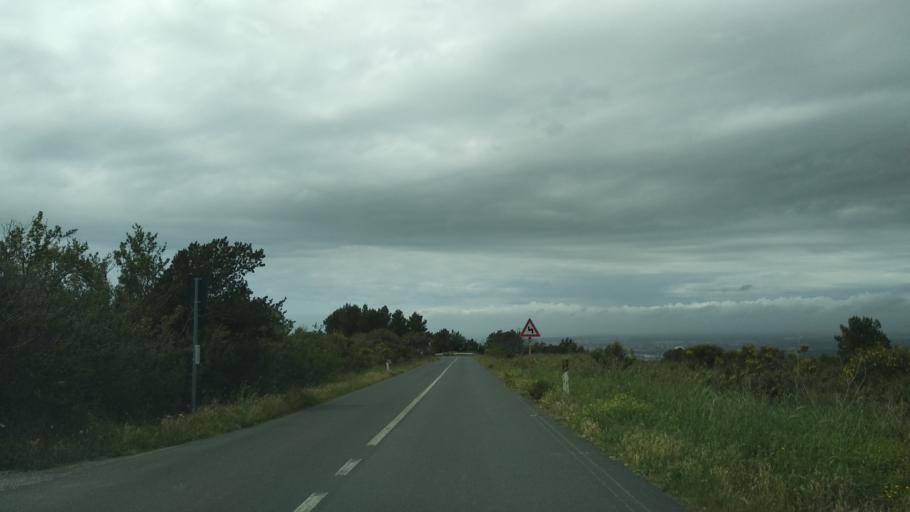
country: IT
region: Tuscany
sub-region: Provincia di Livorno
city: Quercianella
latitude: 43.4951
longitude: 10.3597
